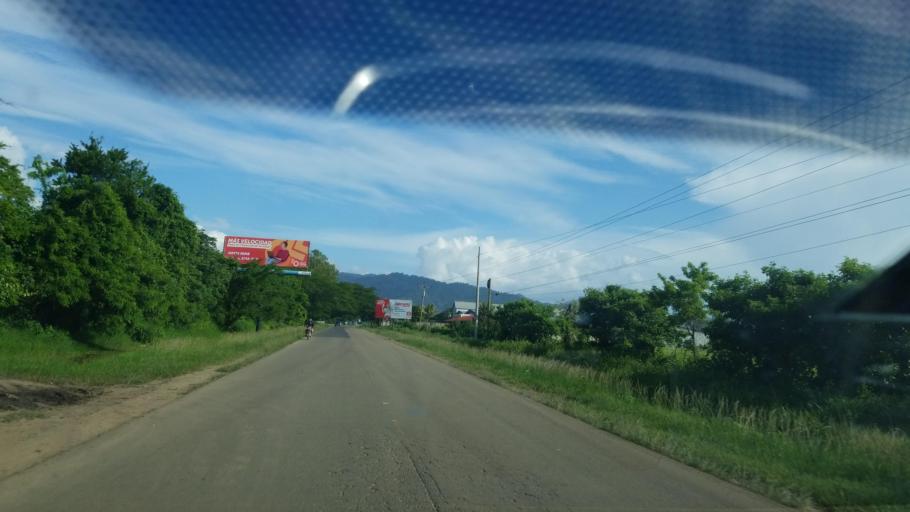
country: HN
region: El Paraiso
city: Cuyali
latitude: 13.8997
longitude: -86.5555
